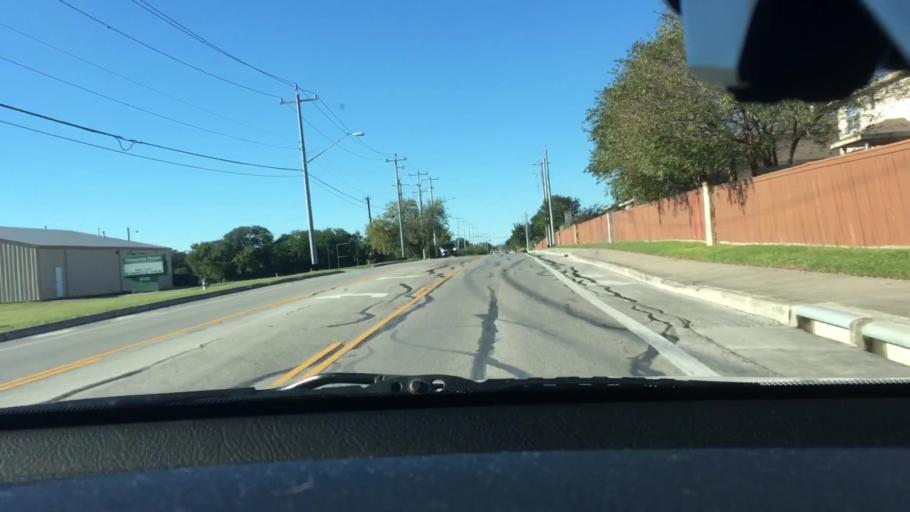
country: US
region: Texas
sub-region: Bexar County
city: Converse
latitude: 29.5300
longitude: -98.3107
